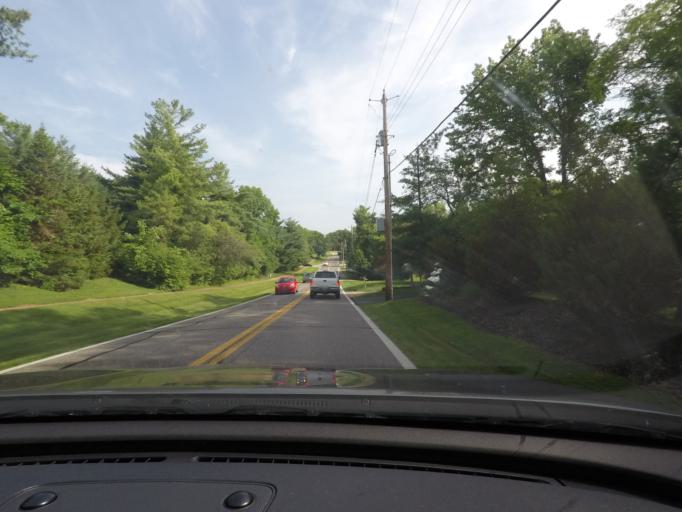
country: US
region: Missouri
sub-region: Saint Louis County
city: Town and Country
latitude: 38.6232
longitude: -90.4828
